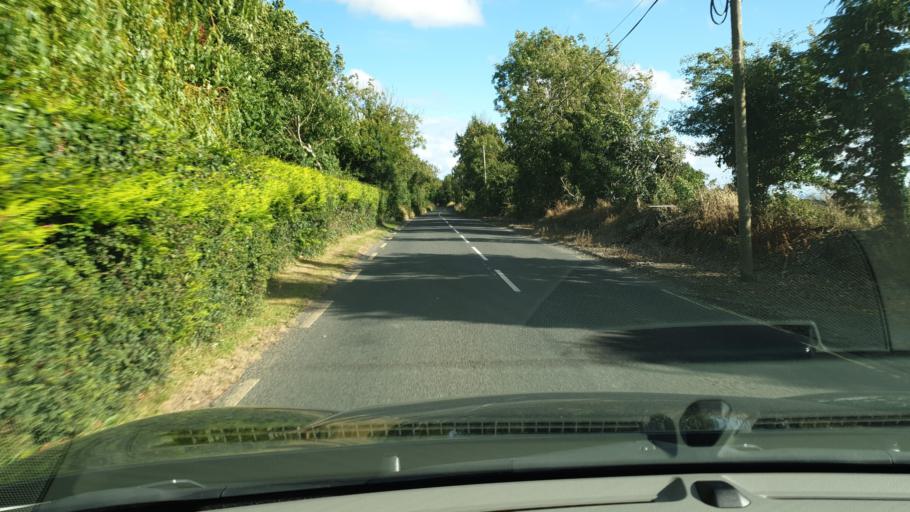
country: IE
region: Leinster
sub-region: An Mhi
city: Ashbourne
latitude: 53.4740
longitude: -6.4237
